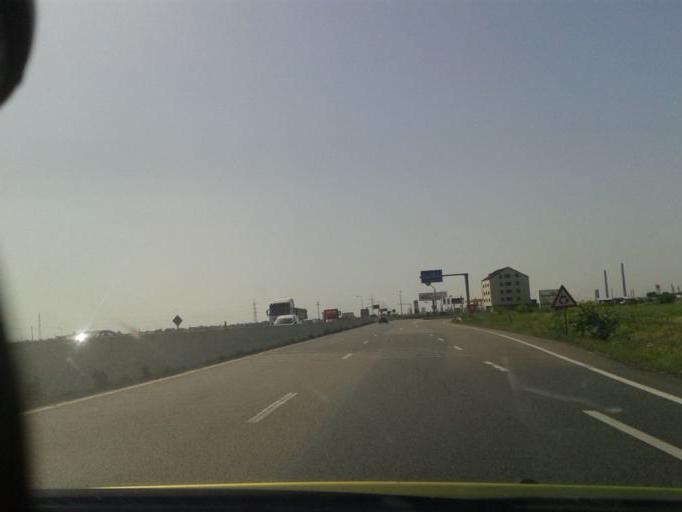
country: RO
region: Prahova
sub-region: Comuna Brazi
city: Negoiesti
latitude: 44.9124
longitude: 25.9909
